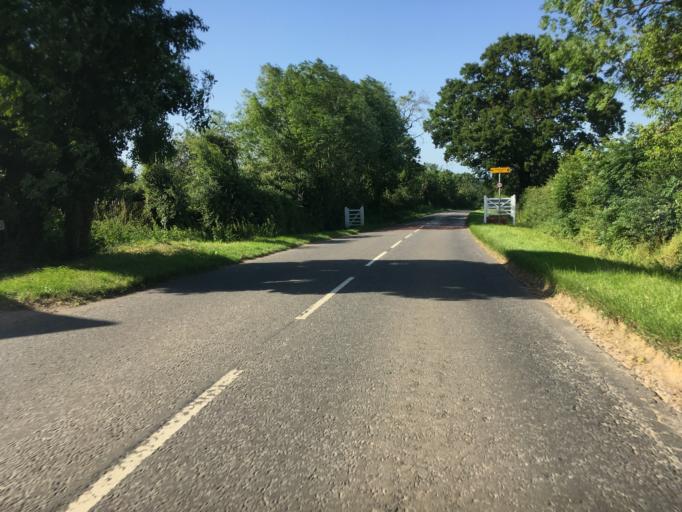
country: GB
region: England
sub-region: Buckinghamshire
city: Steeple Claydon
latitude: 51.9394
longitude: -0.9778
